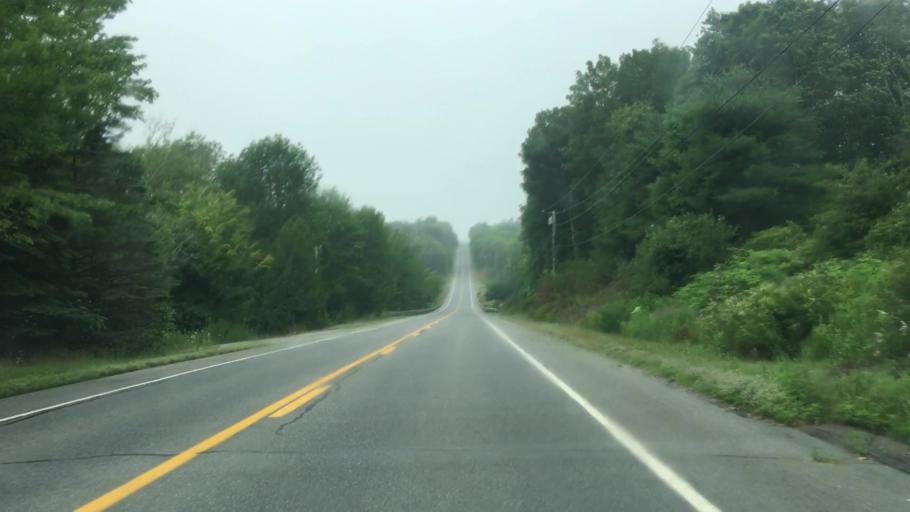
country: US
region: Maine
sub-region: Lincoln County
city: Wiscasset
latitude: 44.0731
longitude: -69.6960
